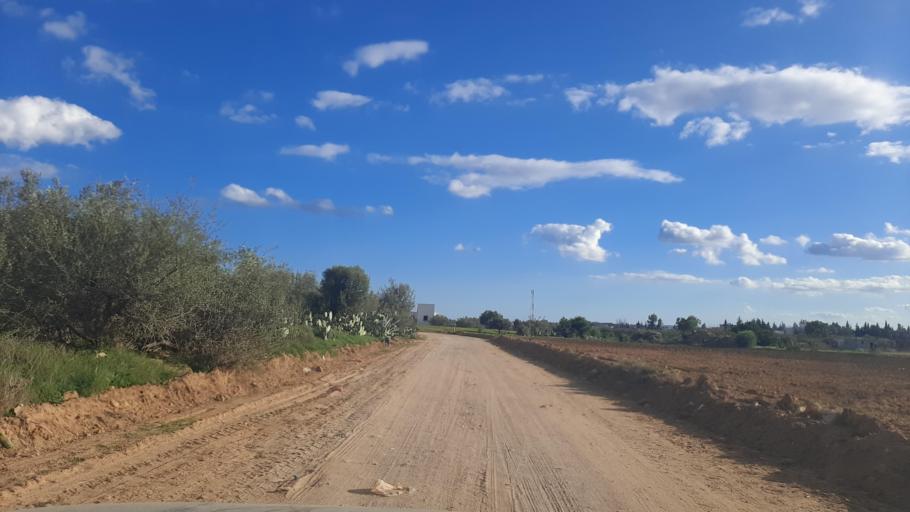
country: TN
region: Nabul
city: Al Hammamat
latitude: 36.4226
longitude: 10.5086
